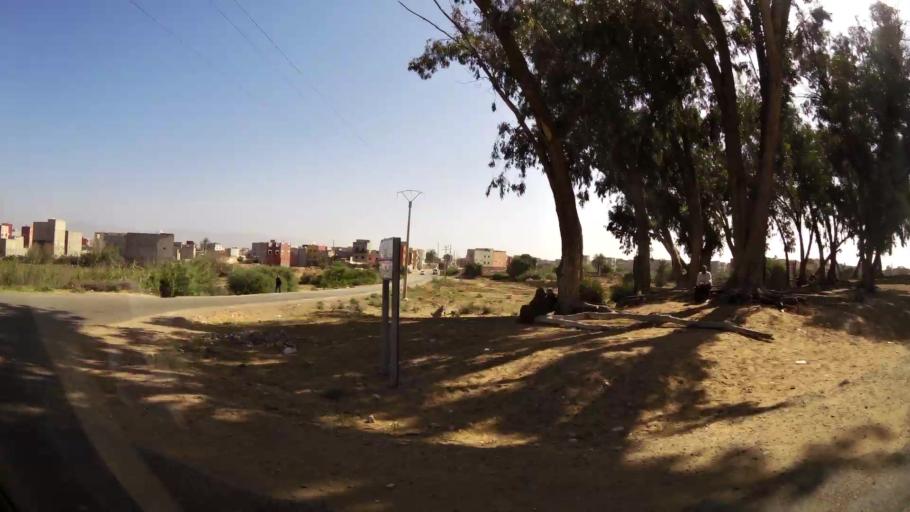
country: MA
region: Souss-Massa-Draa
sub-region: Inezgane-Ait Mellou
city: Inezgane
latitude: 30.3227
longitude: -9.5302
